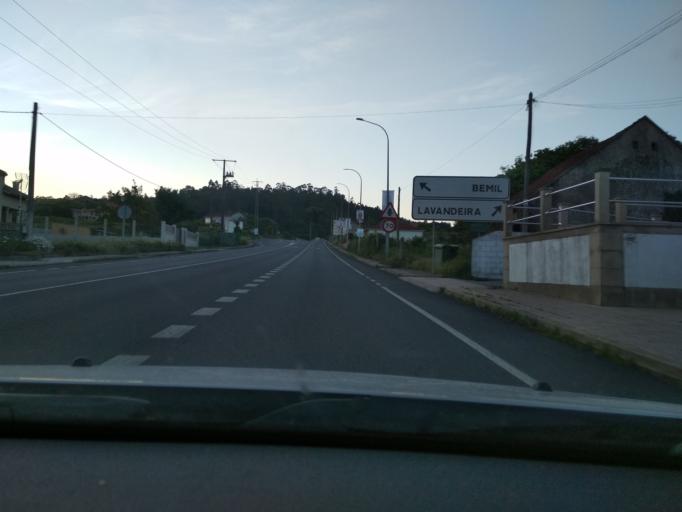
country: ES
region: Galicia
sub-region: Provincia de Pontevedra
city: Caldas de Reis
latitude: 42.6122
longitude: -8.6470
